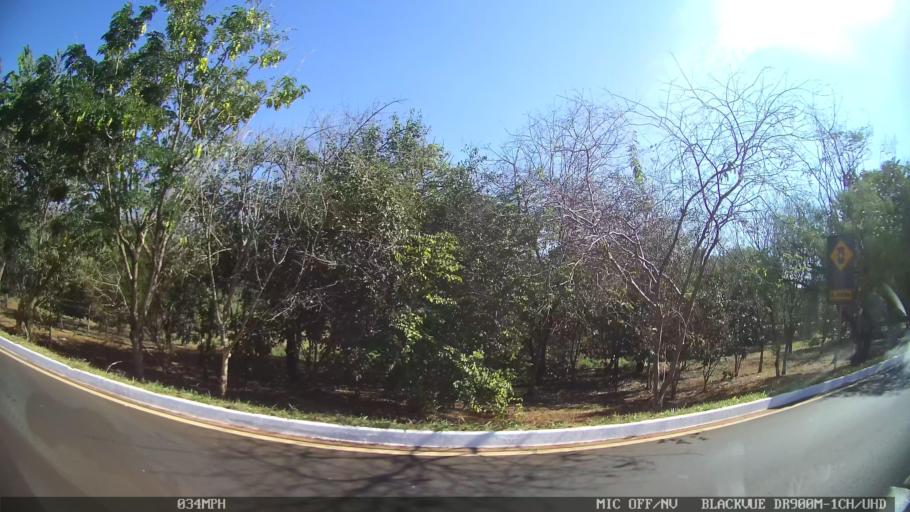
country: BR
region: Sao Paulo
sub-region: Ribeirao Preto
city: Ribeirao Preto
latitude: -21.2290
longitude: -47.7665
